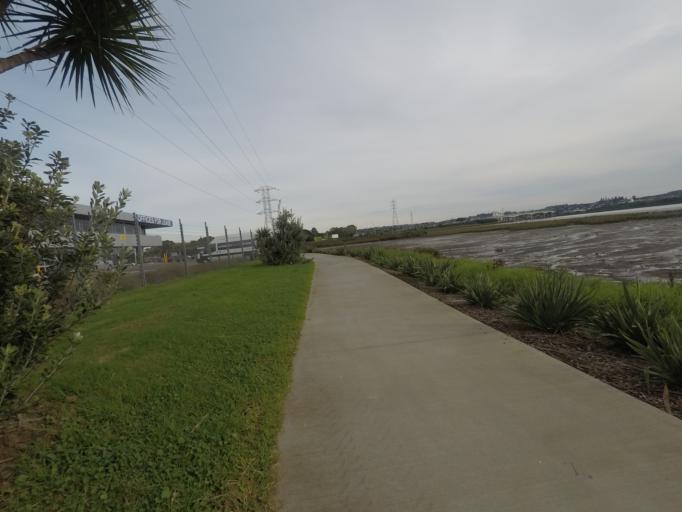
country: NZ
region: Auckland
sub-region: Auckland
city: Mangere
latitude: -36.9417
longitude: 174.7960
